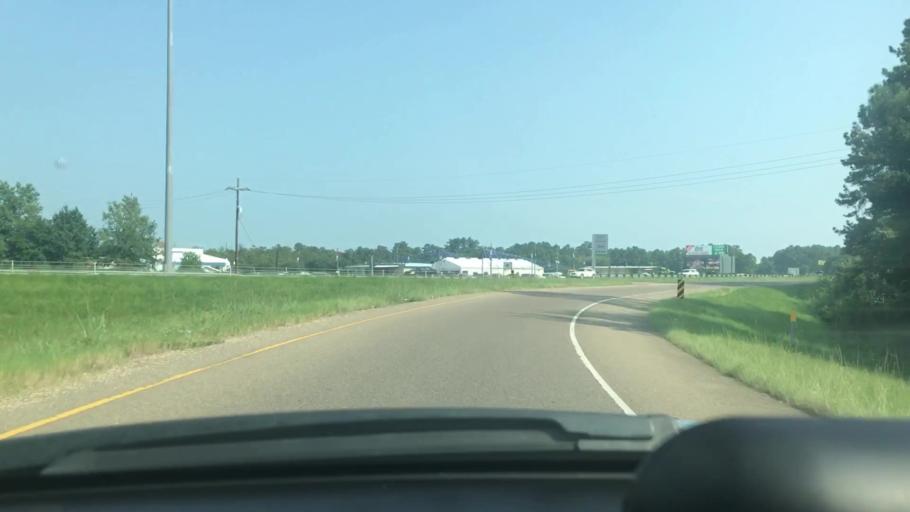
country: US
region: Louisiana
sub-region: Tangipahoa Parish
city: Hammond
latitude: 30.5018
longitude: -90.5042
